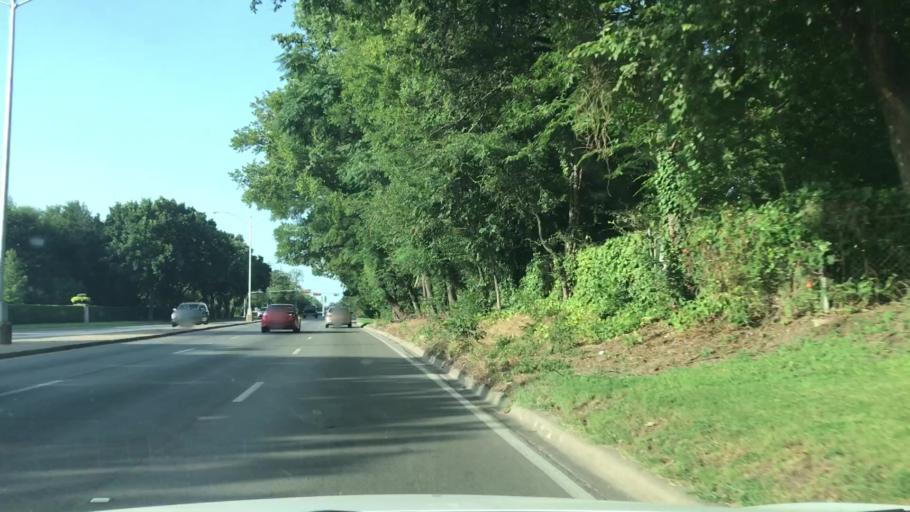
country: US
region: Texas
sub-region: Dallas County
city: Highland Park
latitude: 32.8194
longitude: -96.7177
